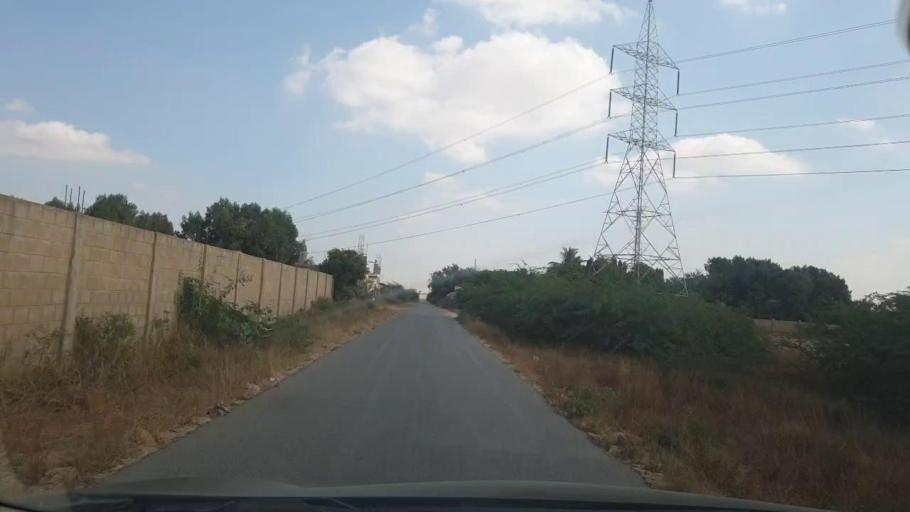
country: PK
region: Sindh
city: Malir Cantonment
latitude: 25.0197
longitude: 67.3654
